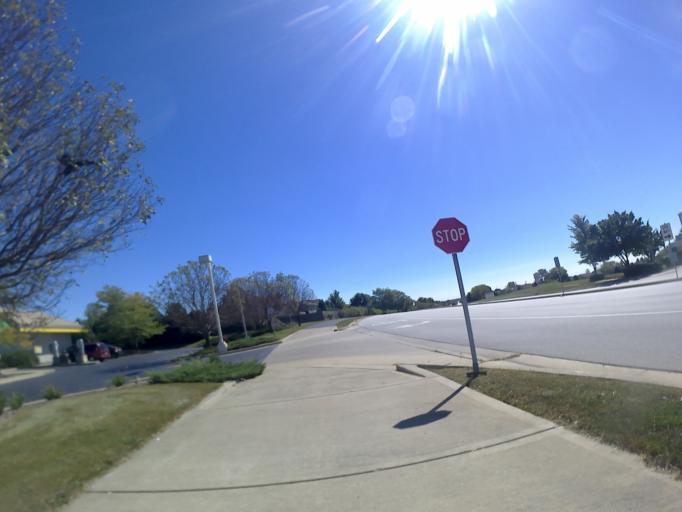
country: US
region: Illinois
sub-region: DuPage County
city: Woodridge
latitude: 41.7273
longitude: -88.0276
